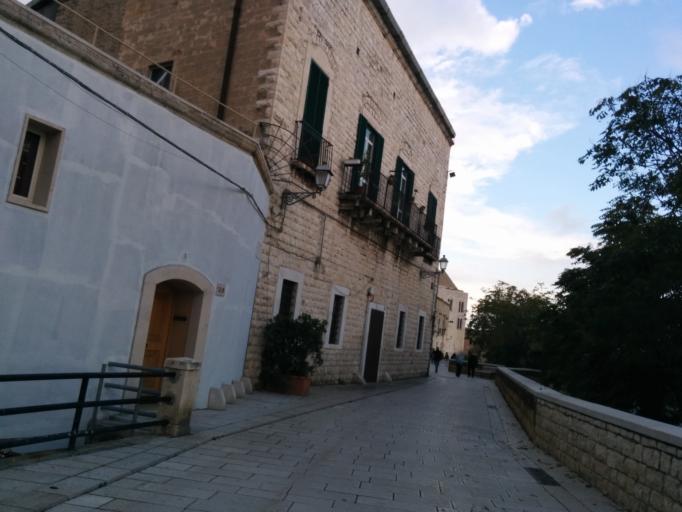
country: IT
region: Apulia
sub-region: Provincia di Bari
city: Bari
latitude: 41.1292
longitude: 16.8720
